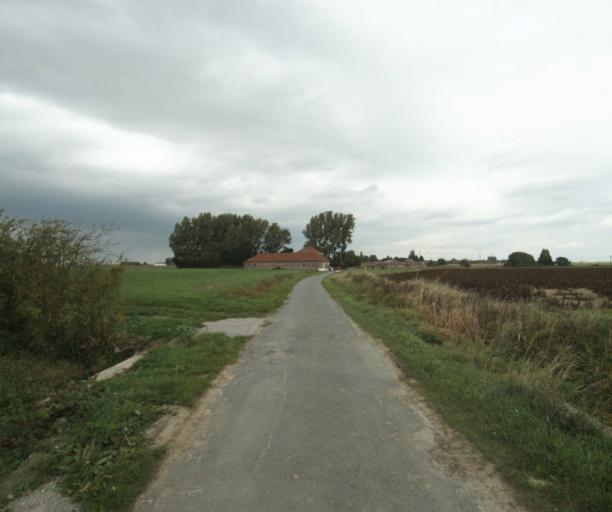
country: FR
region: Nord-Pas-de-Calais
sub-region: Departement du Nord
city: Illies
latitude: 50.5503
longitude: 2.8371
